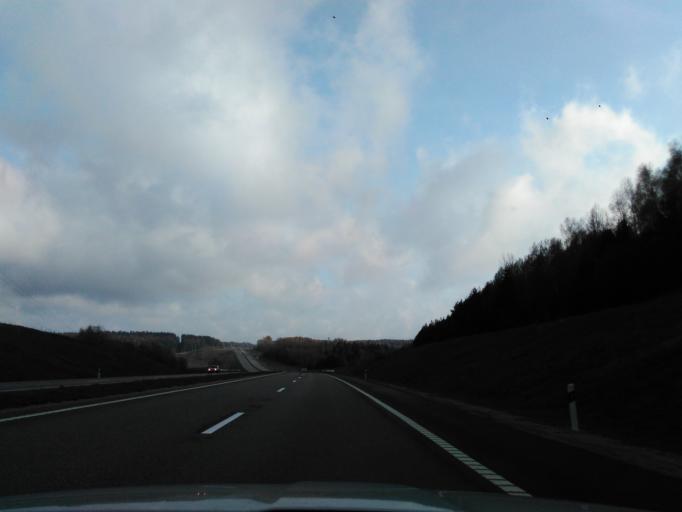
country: BY
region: Minsk
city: Lahoysk
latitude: 54.1920
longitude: 27.8156
